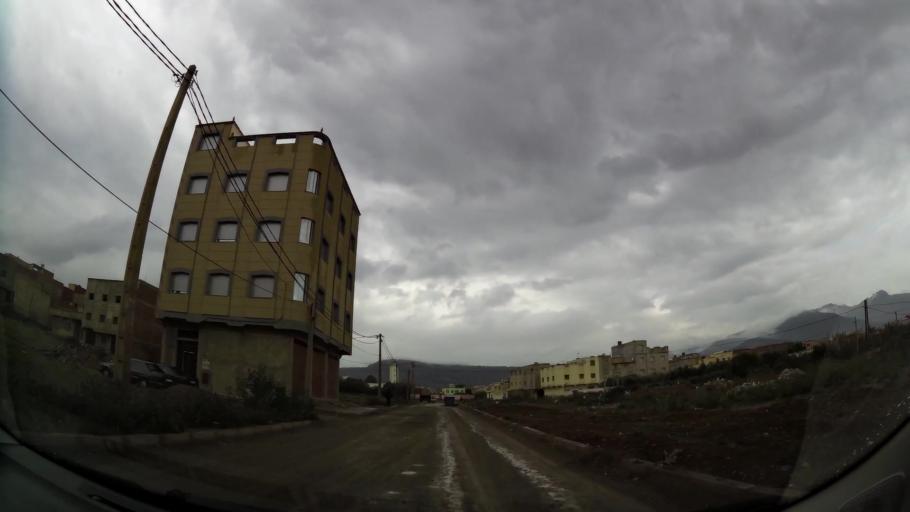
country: MA
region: Oriental
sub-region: Nador
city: Nador
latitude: 35.1477
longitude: -2.9805
